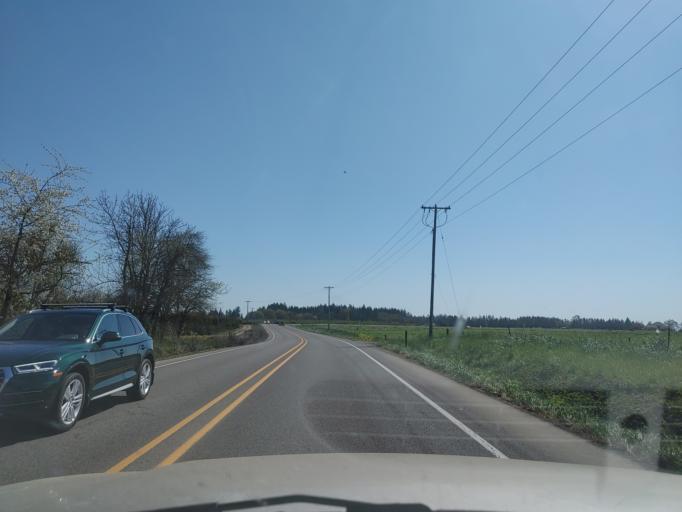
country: US
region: Oregon
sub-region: Yamhill County
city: Newberg
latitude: 45.2501
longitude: -122.9424
